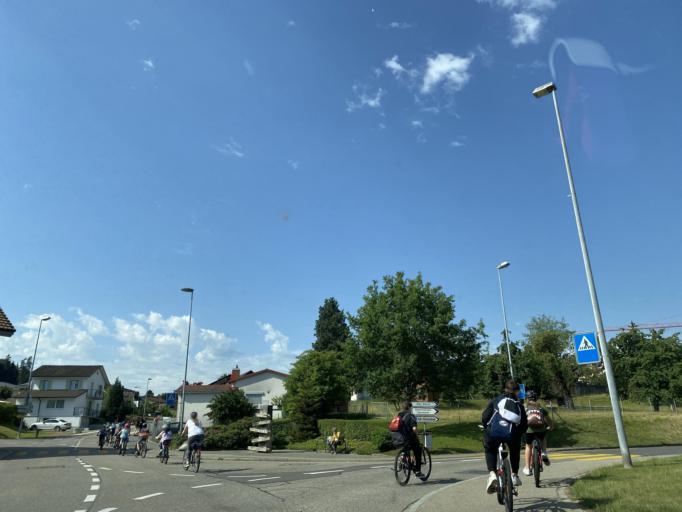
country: CH
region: Aargau
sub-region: Bezirk Zofingen
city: Rothrist
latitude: 47.3040
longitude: 7.8872
